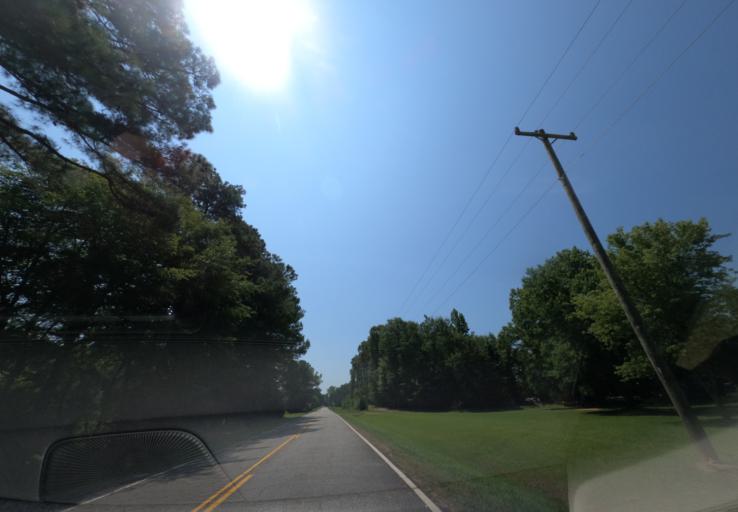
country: US
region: South Carolina
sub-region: Greenwood County
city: Greenwood
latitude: 34.0476
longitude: -82.1354
